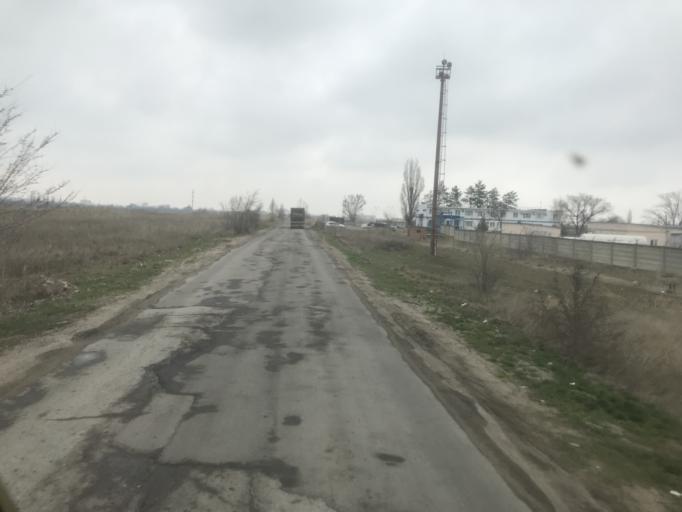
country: RU
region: Volgograd
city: Svetlyy Yar
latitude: 48.5150
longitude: 44.6321
